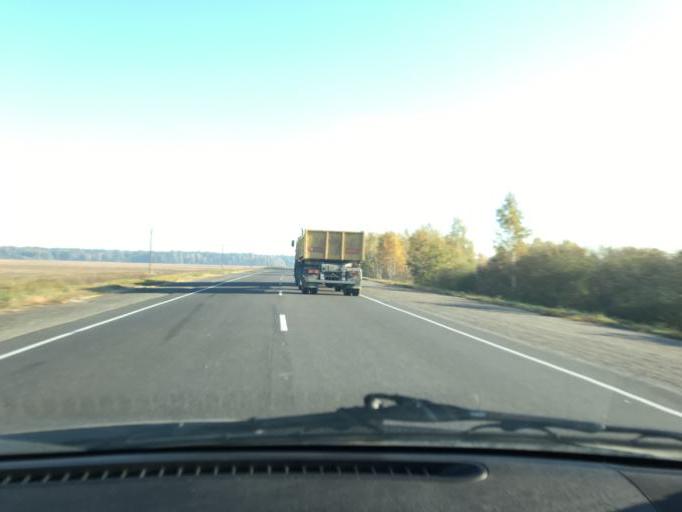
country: BY
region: Brest
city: Asnyezhytsy
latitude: 52.2215
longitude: 26.1318
